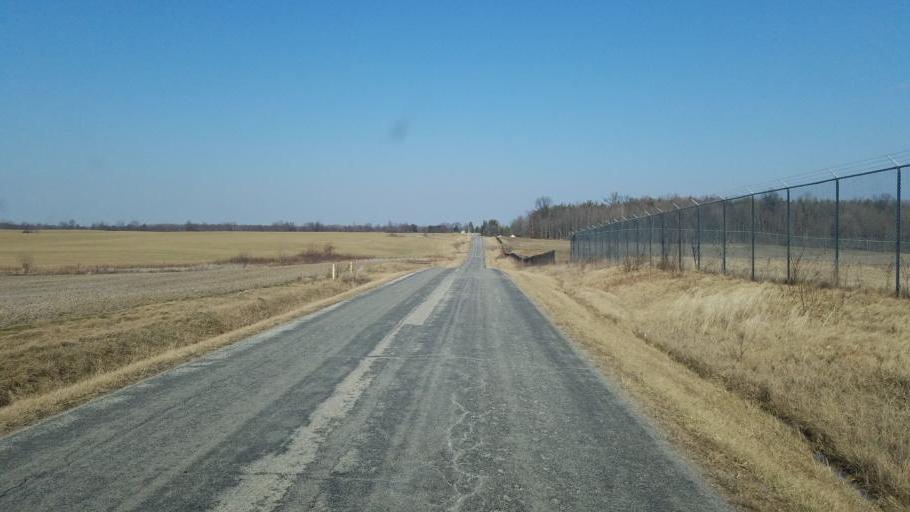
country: US
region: Ohio
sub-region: Richland County
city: Mansfield
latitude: 40.8358
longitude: -82.5328
